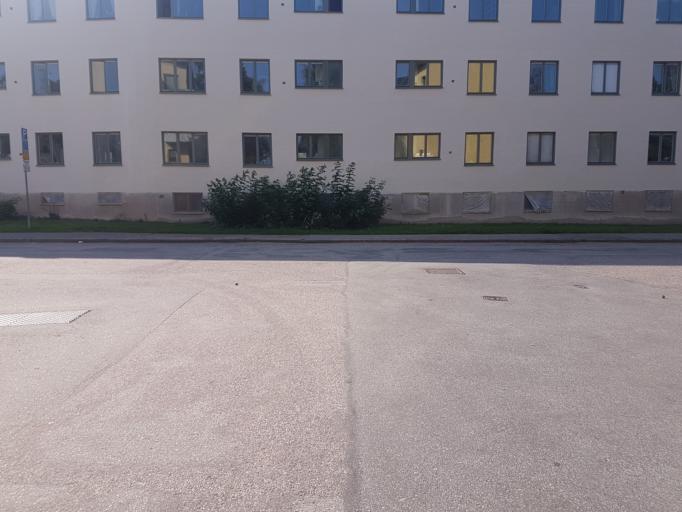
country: SE
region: Stockholm
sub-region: Stockholms Kommun
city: OEstermalm
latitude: 59.2978
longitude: 18.0976
